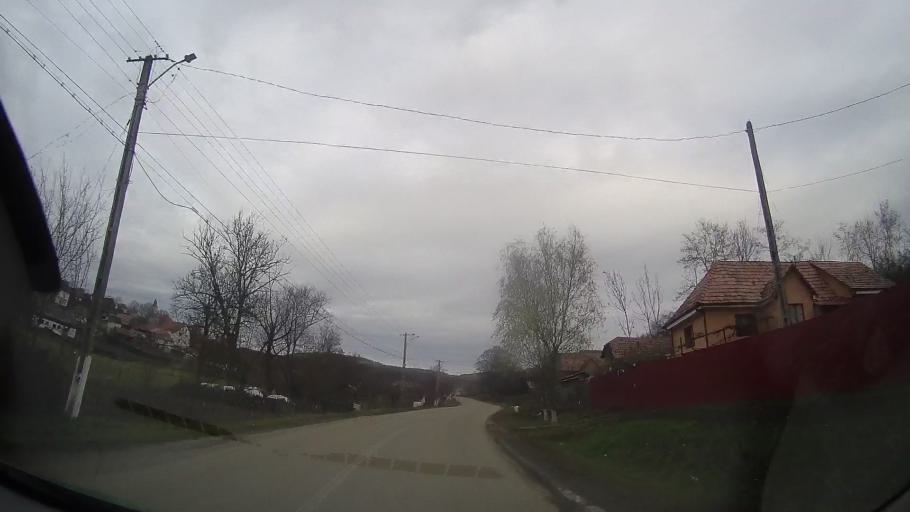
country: RO
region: Mures
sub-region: Comuna Faragau
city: Faragau
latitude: 46.7593
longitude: 24.5171
